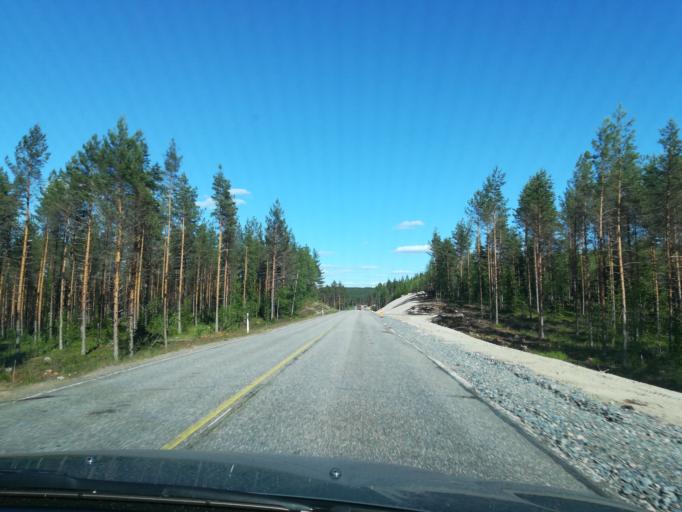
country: FI
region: Southern Savonia
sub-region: Mikkeli
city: Puumala
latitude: 61.4652
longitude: 28.3702
